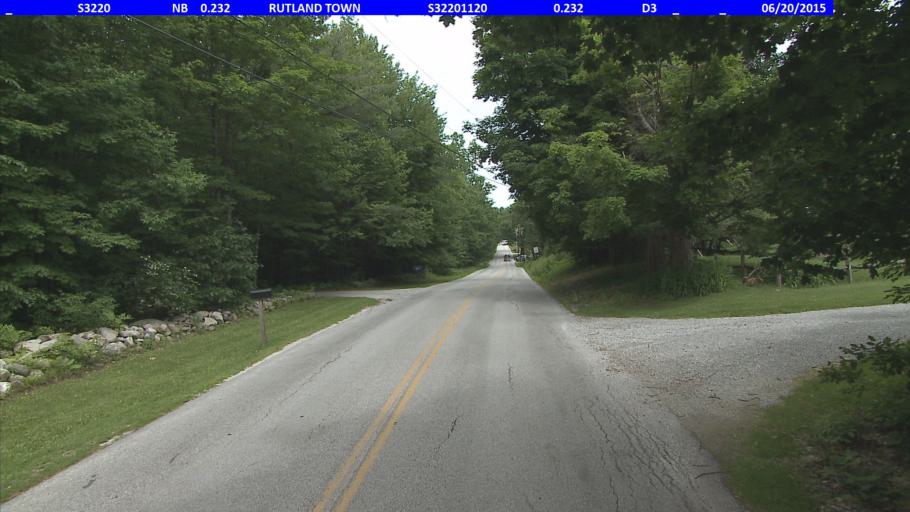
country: US
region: Vermont
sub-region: Rutland County
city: Rutland
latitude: 43.6121
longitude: -72.9362
